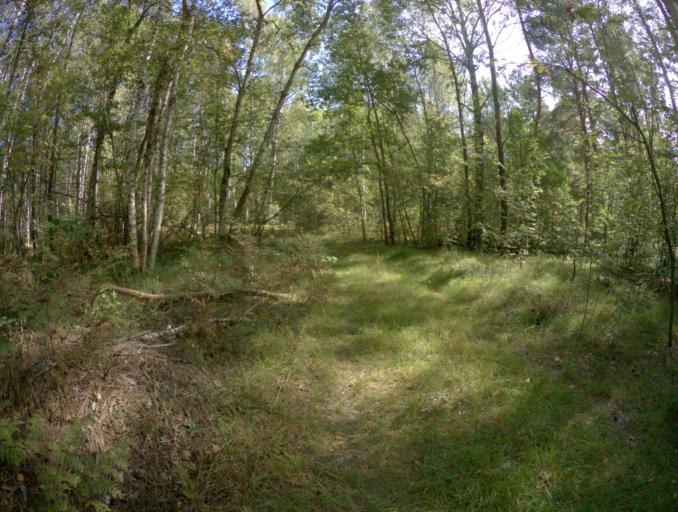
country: RU
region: Vladimir
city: Pokrov
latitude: 55.8444
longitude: 39.2064
